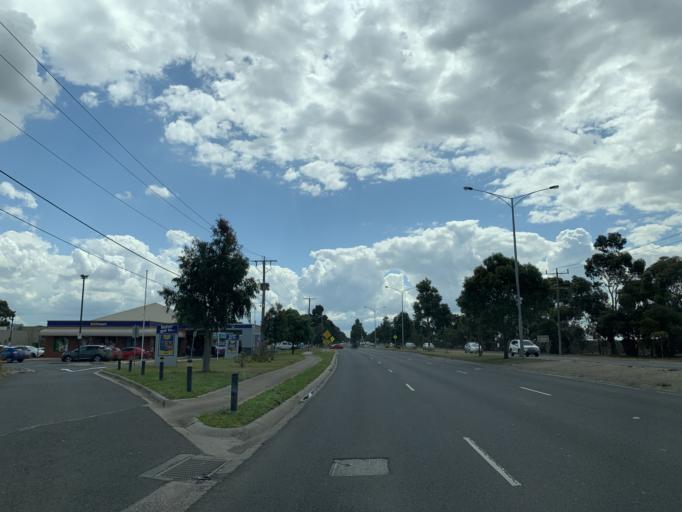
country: AU
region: Victoria
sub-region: Brimbank
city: Kealba
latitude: -37.7473
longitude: 144.8301
